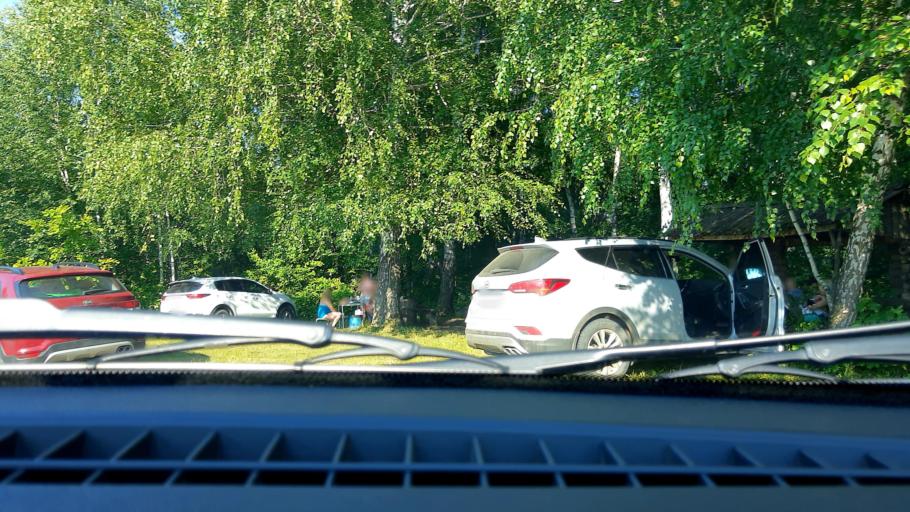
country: RU
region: Bashkortostan
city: Mikhaylovka
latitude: 54.8313
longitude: 55.8591
